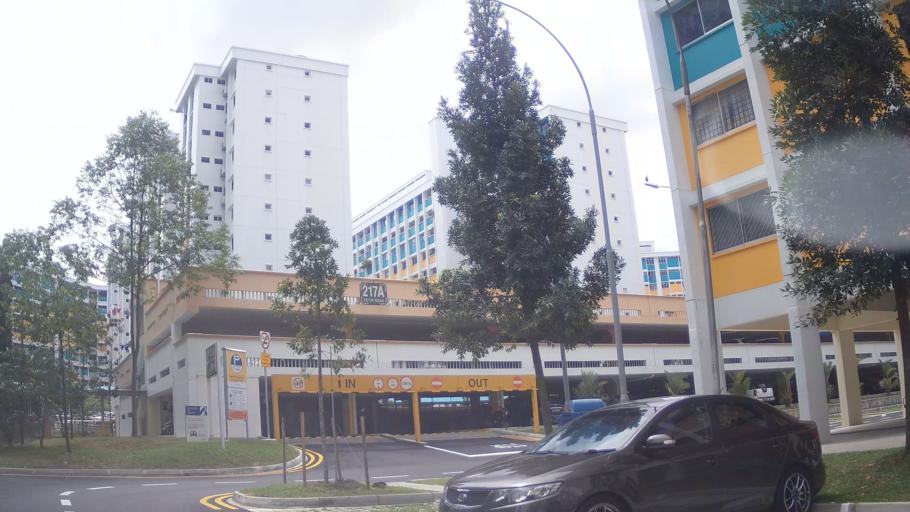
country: MY
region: Johor
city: Johor Bahru
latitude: 1.3747
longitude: 103.7742
